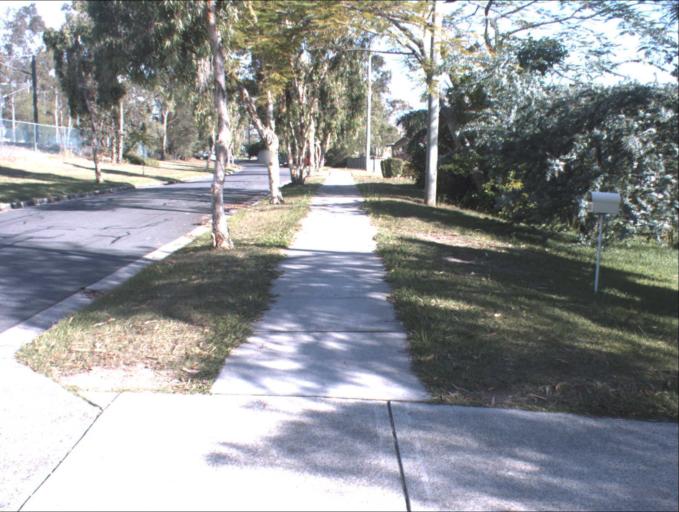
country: AU
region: Queensland
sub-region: Logan
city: Woodridge
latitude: -27.6236
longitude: 153.0978
